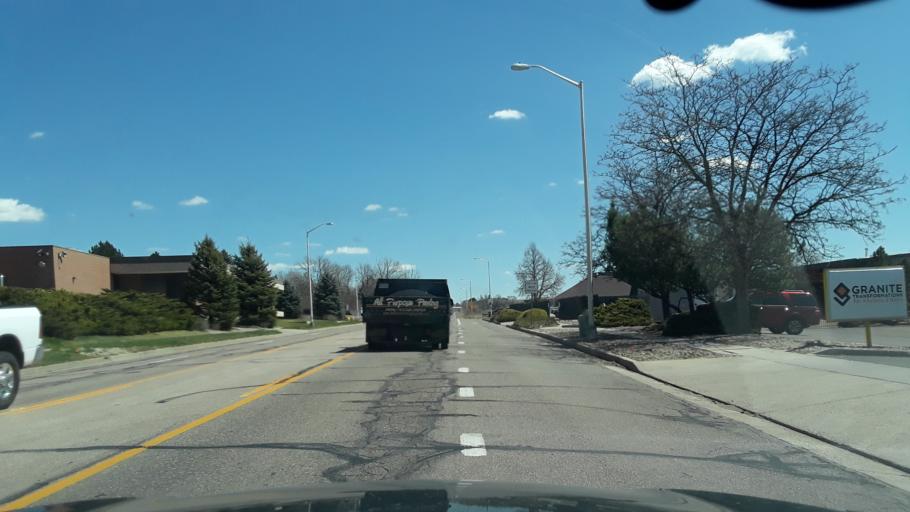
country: US
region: Colorado
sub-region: El Paso County
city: Cimarron Hills
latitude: 38.8467
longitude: -104.7310
